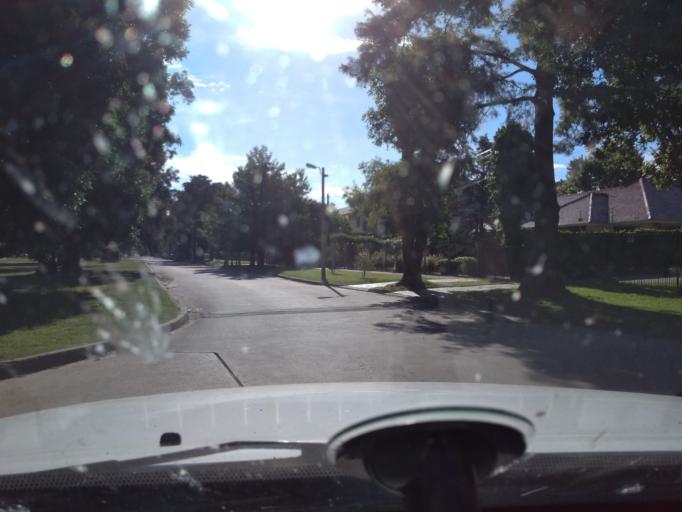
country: UY
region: Canelones
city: Paso de Carrasco
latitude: -34.8874
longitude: -56.0664
